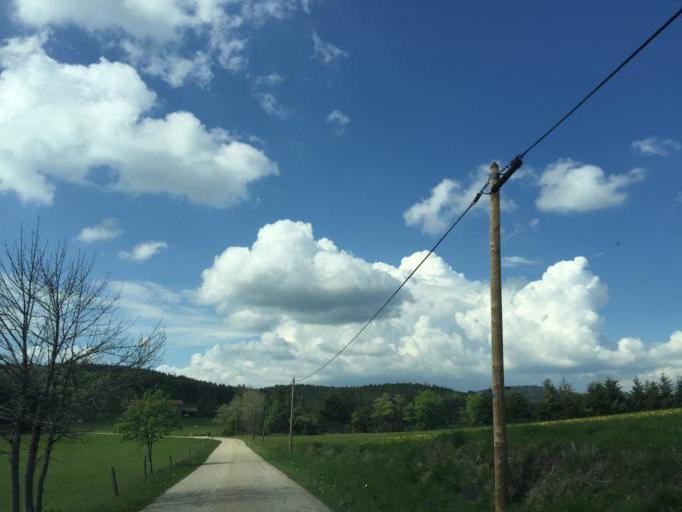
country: FR
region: Rhone-Alpes
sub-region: Departement de la Loire
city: Saint-Sauveur-en-Rue
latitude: 45.3032
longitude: 4.4787
